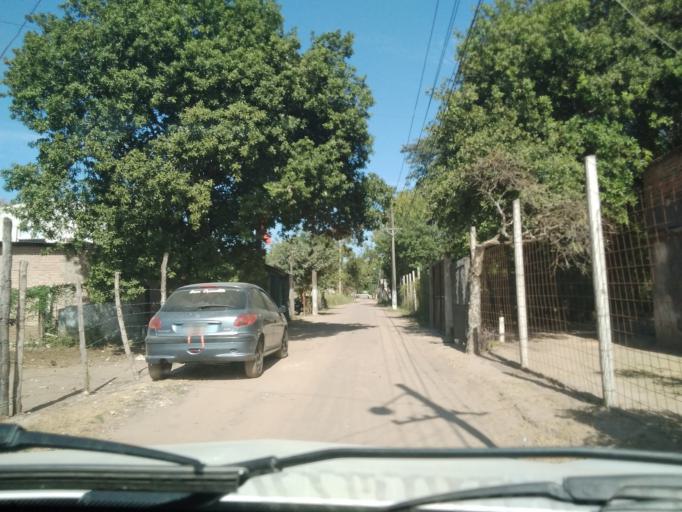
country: AR
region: Corrientes
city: Corrientes
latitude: -27.5140
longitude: -58.8039
